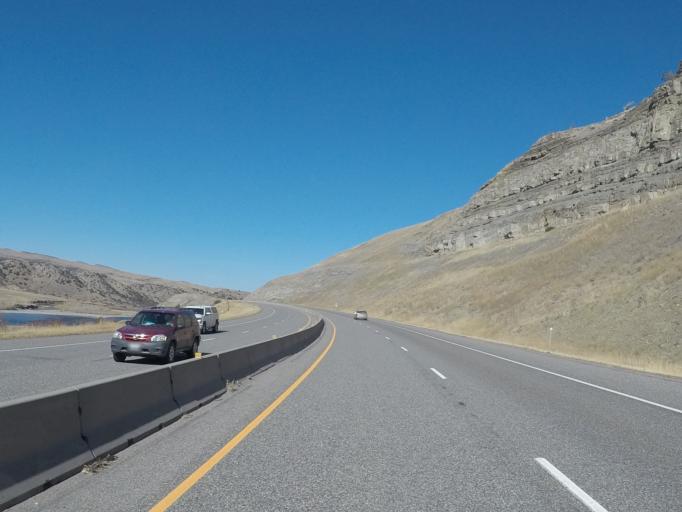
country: US
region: Montana
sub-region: Park County
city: Livingston
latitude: 45.7047
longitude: -110.2602
